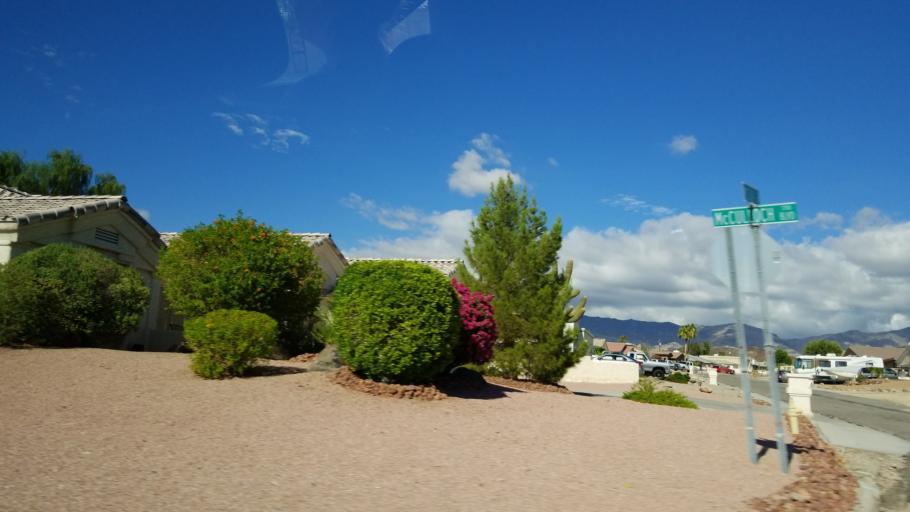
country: US
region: Arizona
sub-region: Mohave County
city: Lake Havasu City
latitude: 34.4992
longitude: -114.2783
